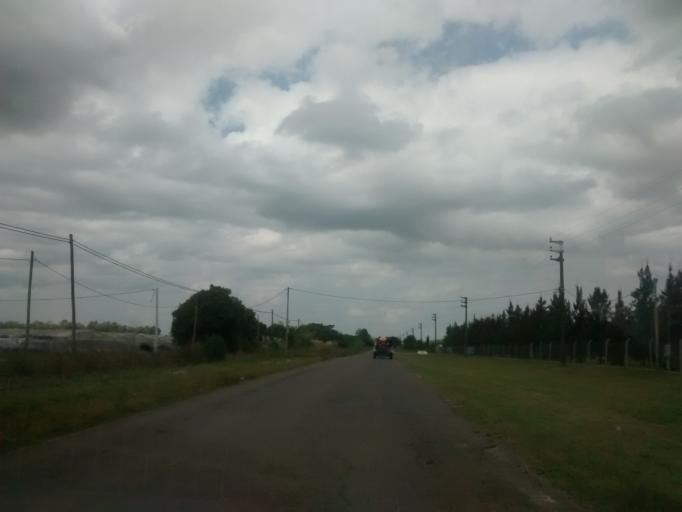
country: AR
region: Buenos Aires
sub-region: Partido de La Plata
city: La Plata
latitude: -34.9841
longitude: -57.9260
